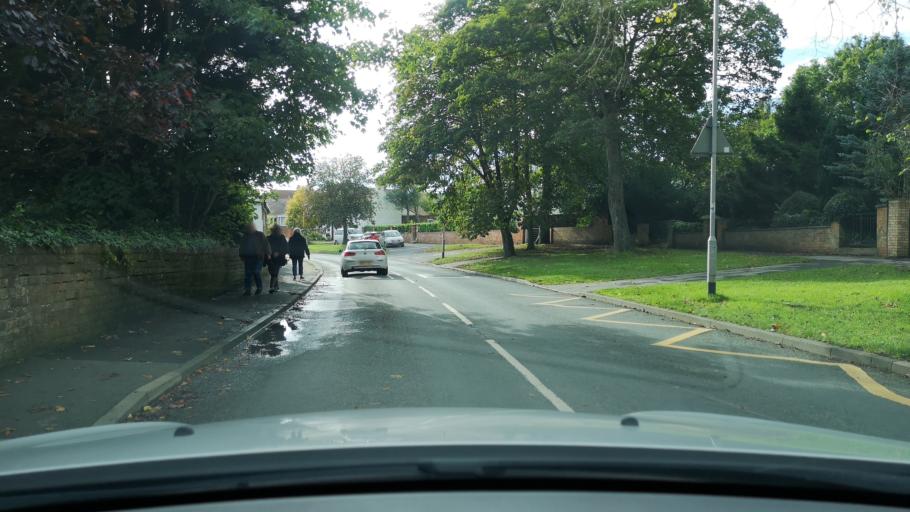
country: GB
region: England
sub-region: East Riding of Yorkshire
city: Hornsea
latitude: 53.9129
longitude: -0.1741
